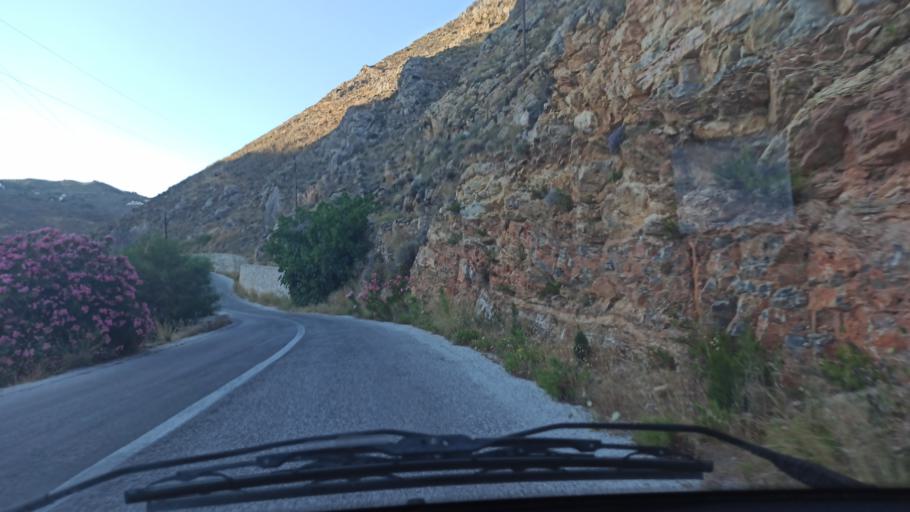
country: GR
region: South Aegean
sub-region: Nomos Kykladon
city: Ano Syros
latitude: 37.4547
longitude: 24.9335
